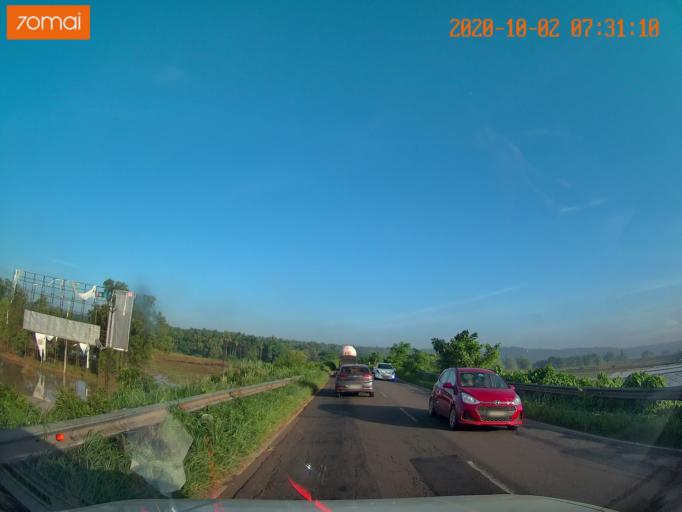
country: IN
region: Kerala
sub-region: Malappuram
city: Pariyapuram
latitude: 11.0475
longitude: 75.9395
